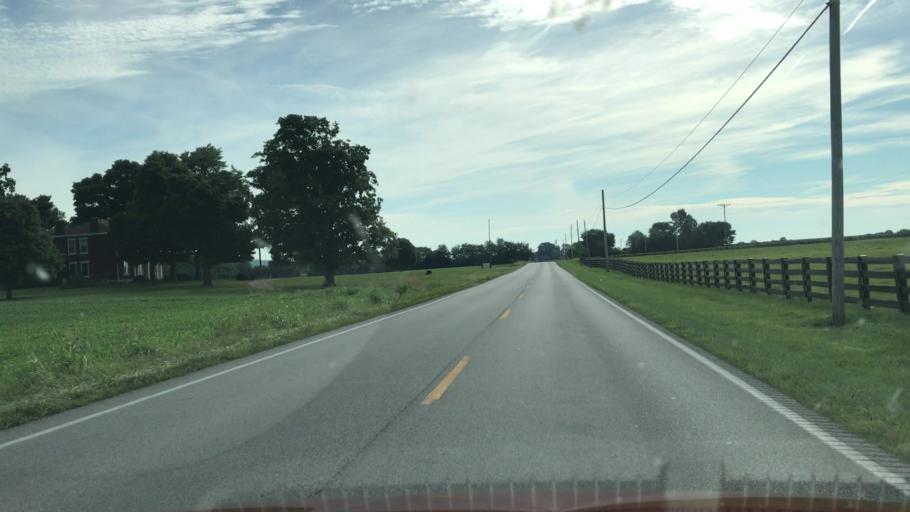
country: US
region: Kentucky
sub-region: Edmonson County
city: Brownsville
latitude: 37.0648
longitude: -86.2821
